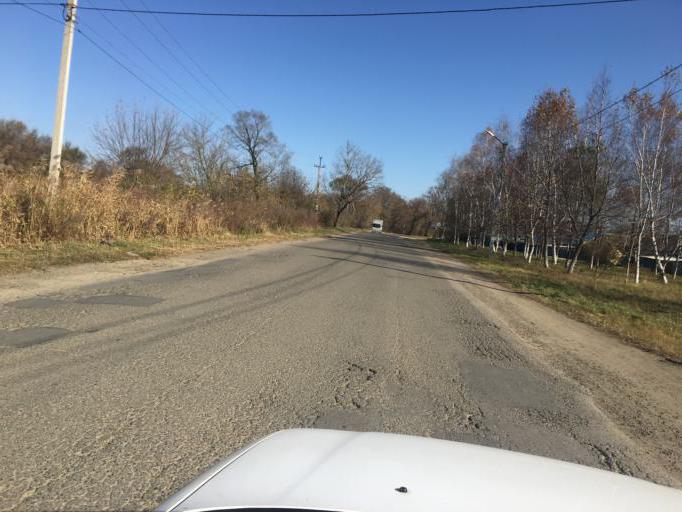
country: RU
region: Primorskiy
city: Dal'nerechensk
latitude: 45.9328
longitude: 133.7514
